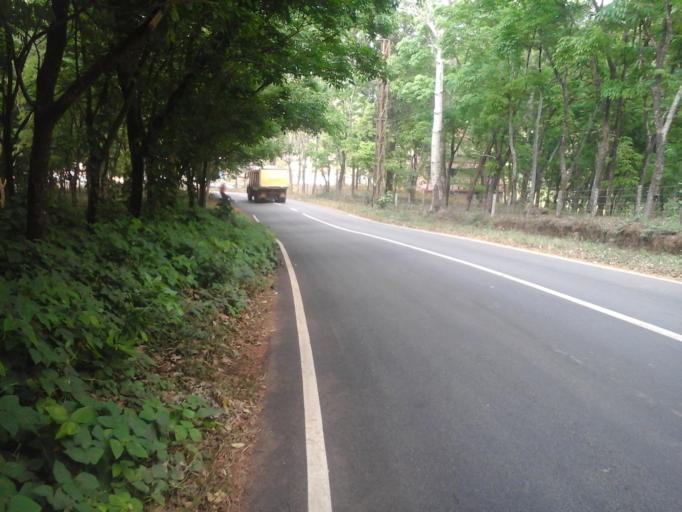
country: IN
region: Kerala
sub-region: Kannur
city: Taliparamba
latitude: 12.1439
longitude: 75.4419
